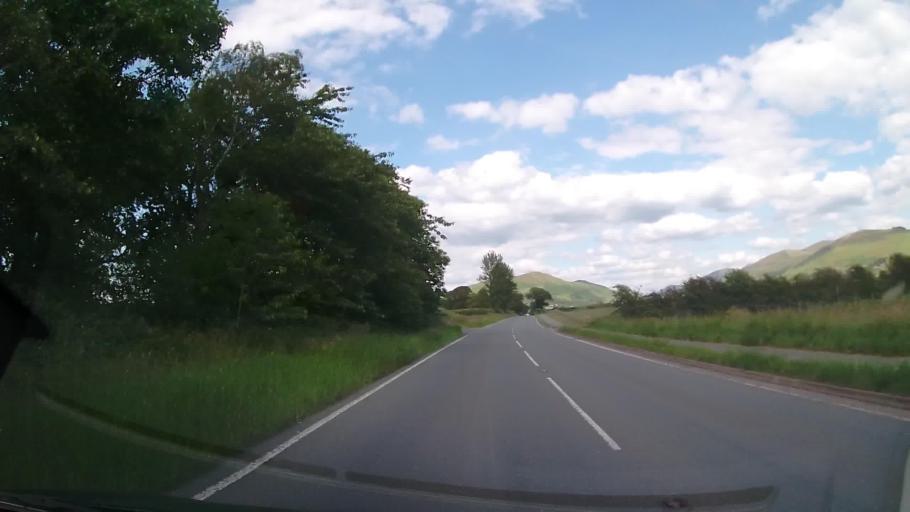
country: GB
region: Wales
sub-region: Gwynedd
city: Tywyn
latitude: 52.5957
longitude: -4.0707
